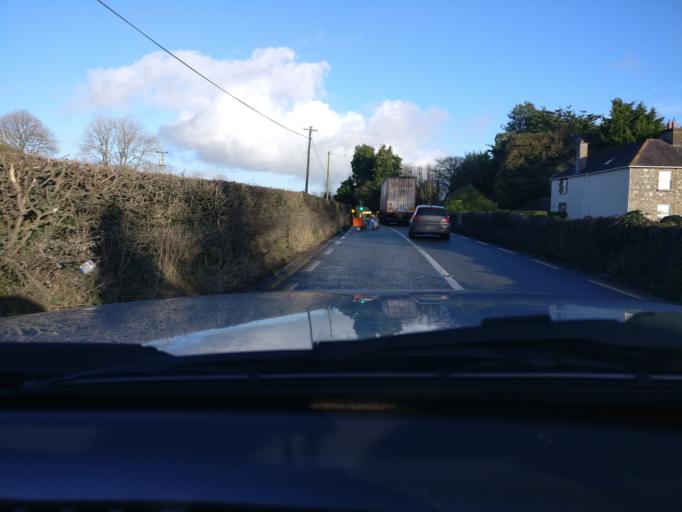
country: IE
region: Leinster
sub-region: An Iarmhi
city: Rathwire
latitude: 53.5805
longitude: -7.1518
